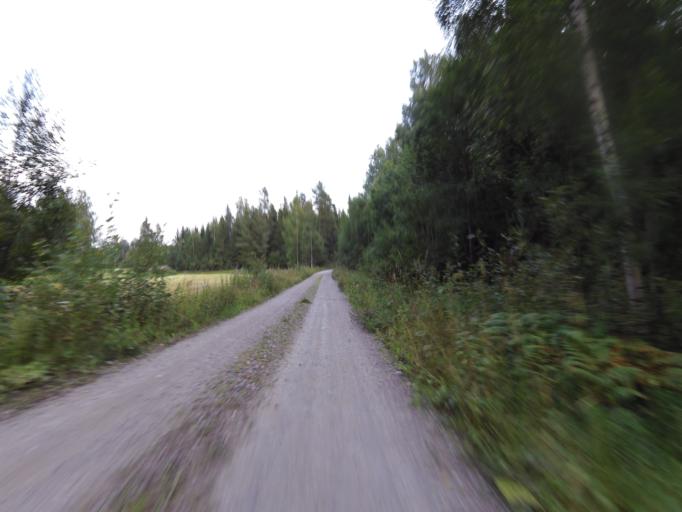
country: SE
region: Gaevleborg
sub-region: Gavle Kommun
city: Gavle
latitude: 60.7092
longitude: 17.1183
